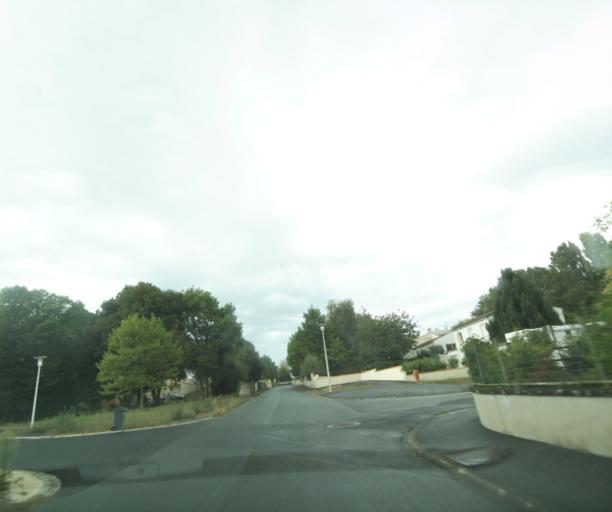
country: FR
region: Poitou-Charentes
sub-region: Departement de la Charente-Maritime
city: Tonnay-Charente
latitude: 45.9452
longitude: -0.8798
